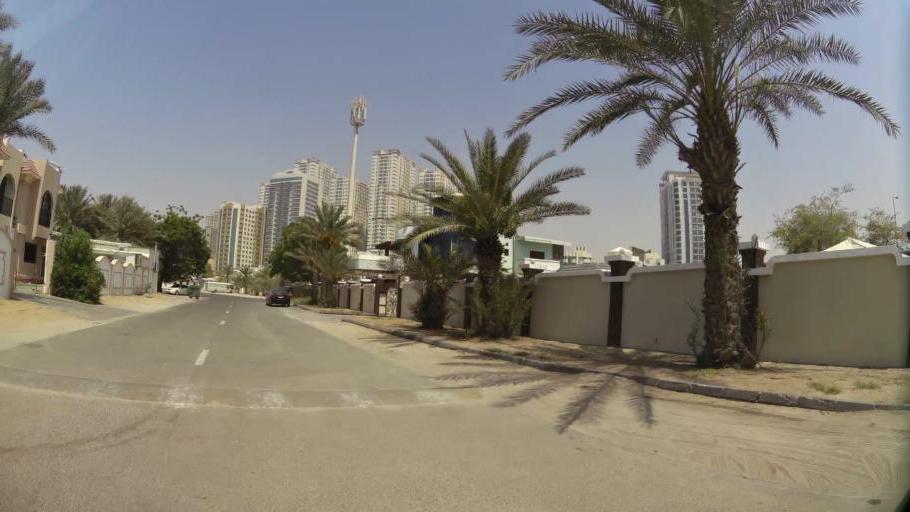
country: AE
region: Ajman
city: Ajman
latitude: 25.3965
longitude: 55.4256
